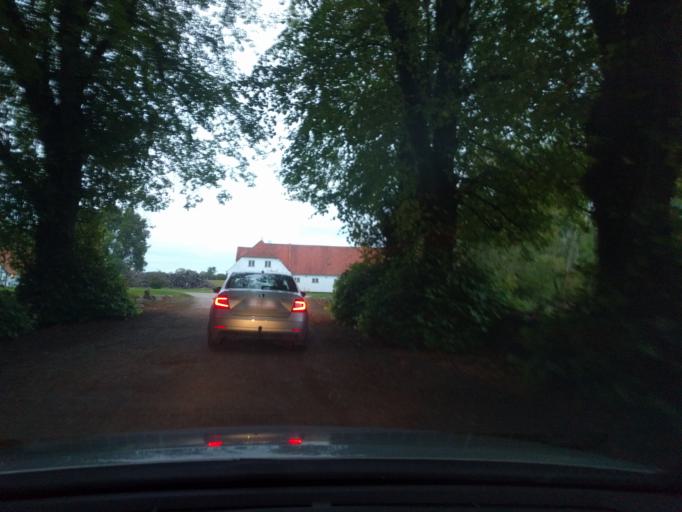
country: DK
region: South Denmark
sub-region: Assens Kommune
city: Tommerup
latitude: 55.2280
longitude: 10.2702
